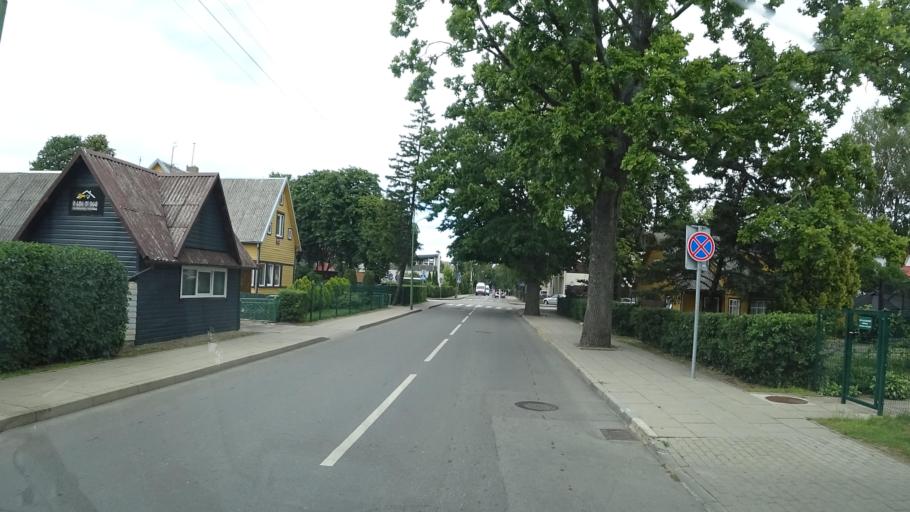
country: LT
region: Klaipedos apskritis
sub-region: Klaipeda
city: Palanga
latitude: 55.9110
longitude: 21.0676
